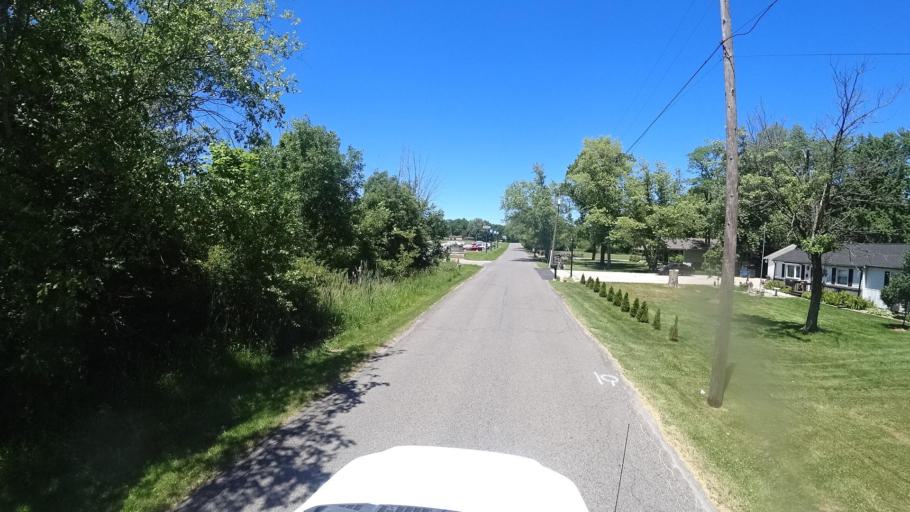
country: US
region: Indiana
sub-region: Porter County
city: Porter
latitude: 41.6300
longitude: -87.0868
